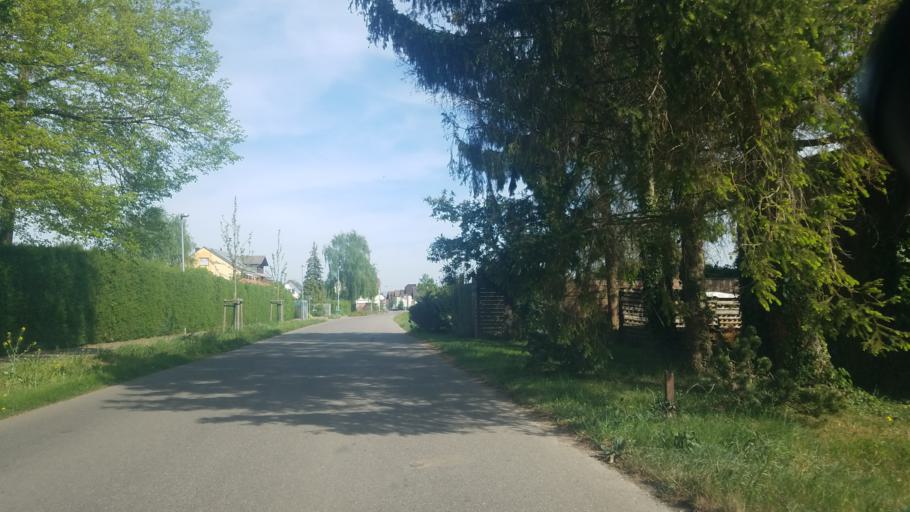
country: DE
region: Baden-Wuerttemberg
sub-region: Freiburg Region
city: Meissenheim
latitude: 48.4388
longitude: 7.7959
